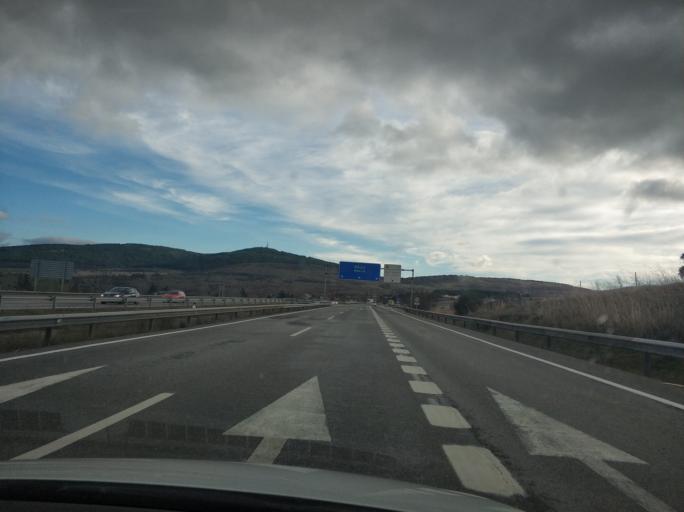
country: ES
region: Madrid
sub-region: Provincia de Madrid
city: Buitrago del Lozoya
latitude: 40.9857
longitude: -3.6409
